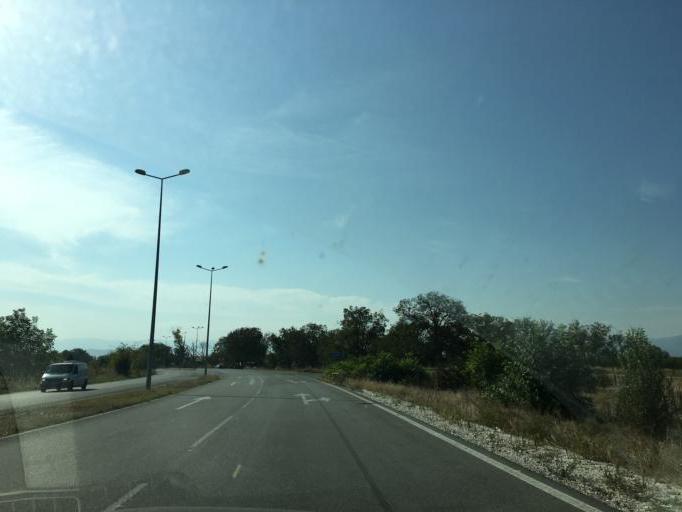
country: BG
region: Pazardzhik
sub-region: Obshtina Pazardzhik
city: Pazardzhik
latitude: 42.2230
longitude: 24.3105
